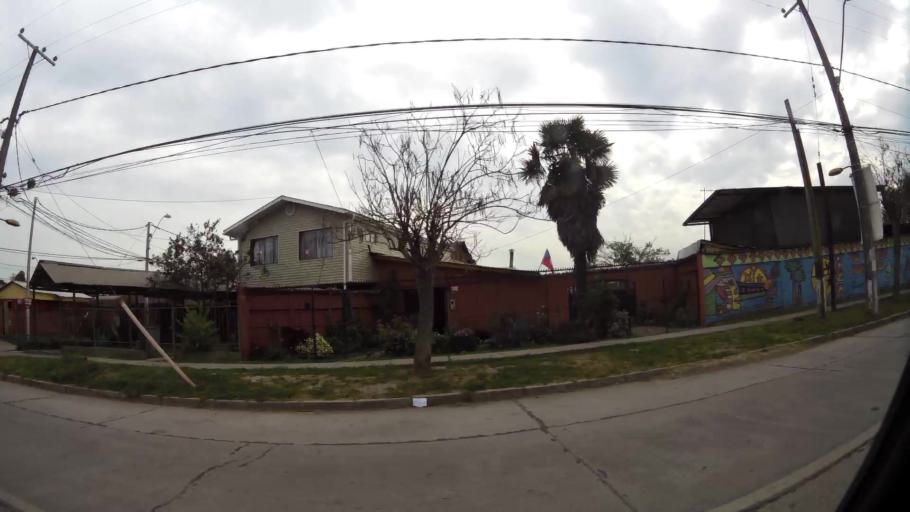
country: CL
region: Santiago Metropolitan
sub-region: Provincia de Santiago
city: Lo Prado
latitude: -33.4988
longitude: -70.7716
